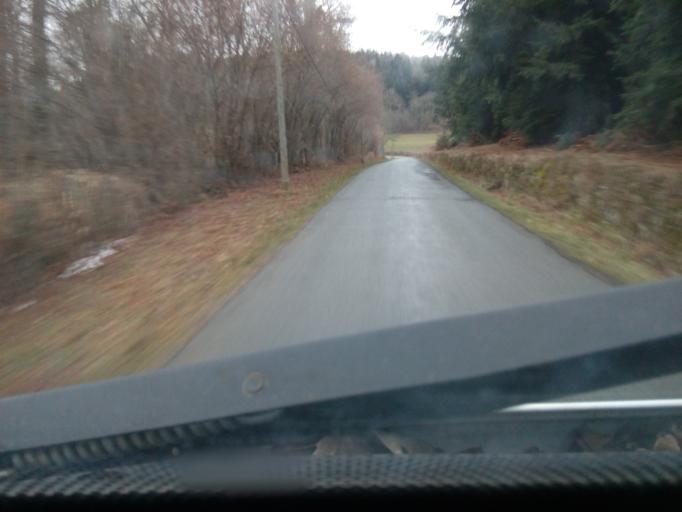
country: FR
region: Limousin
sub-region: Departement de la Creuse
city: Felletin
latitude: 45.8299
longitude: 2.2483
